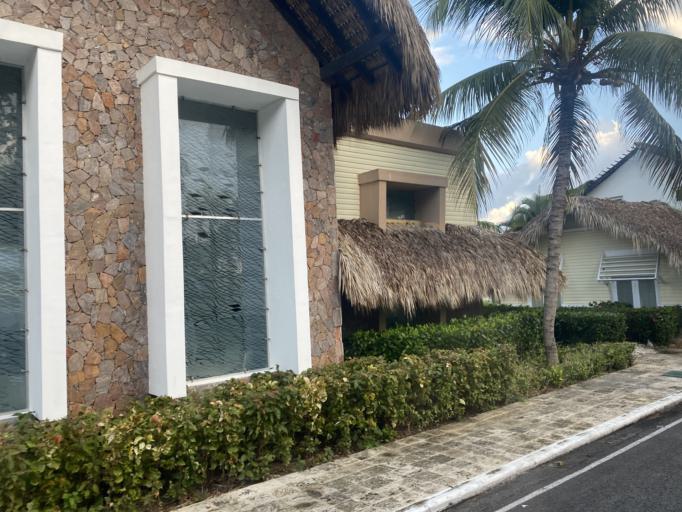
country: DO
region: San Juan
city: Punta Cana
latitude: 18.7281
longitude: -68.4699
